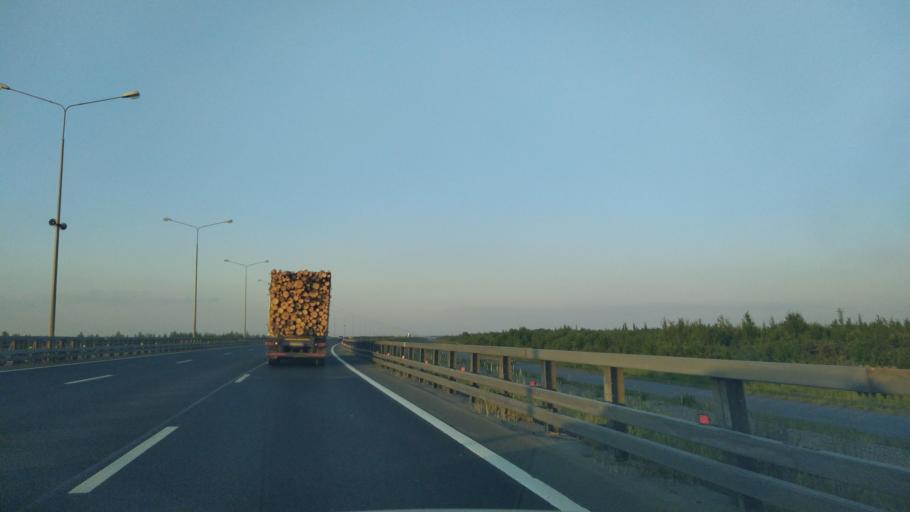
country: RU
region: St.-Petersburg
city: Kronshtadt
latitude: 60.0195
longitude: 29.7351
